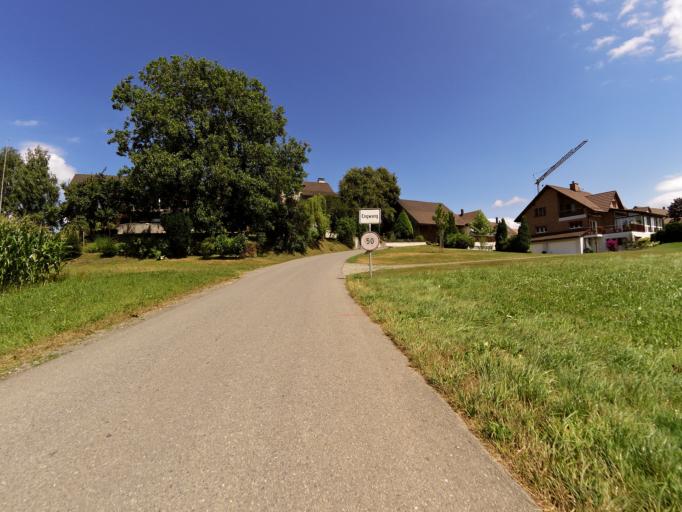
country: CH
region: Thurgau
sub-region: Weinfelden District
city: Wigoltingen
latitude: 47.5995
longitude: 9.0504
